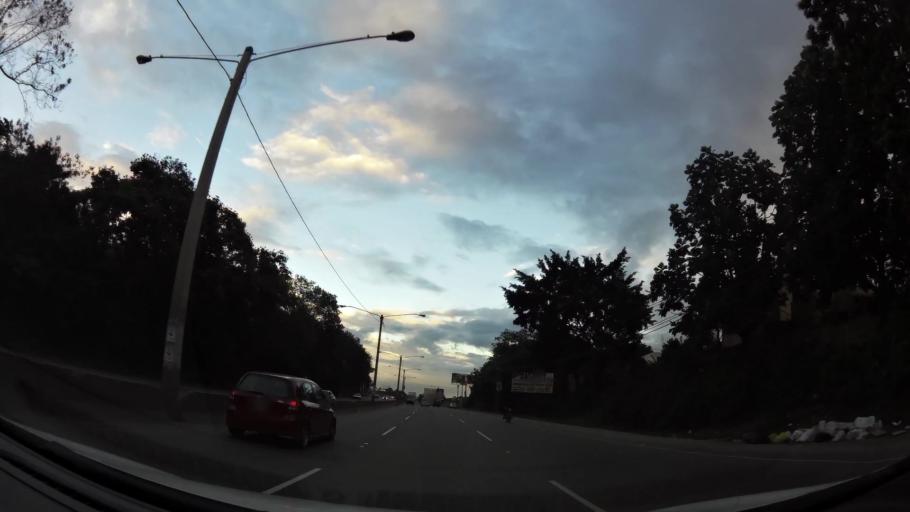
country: DO
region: Santo Domingo
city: Santo Domingo Oeste
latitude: 18.5378
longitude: -70.0240
